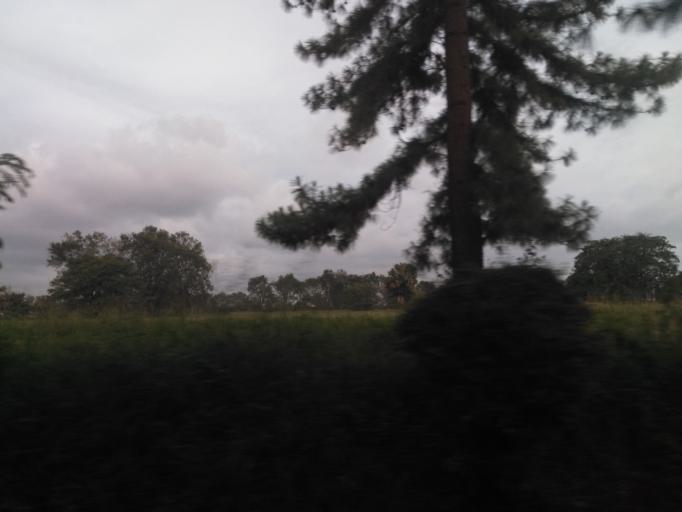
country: UG
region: Eastern Region
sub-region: Jinja District
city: Jinja
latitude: 0.4230
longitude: 33.1978
